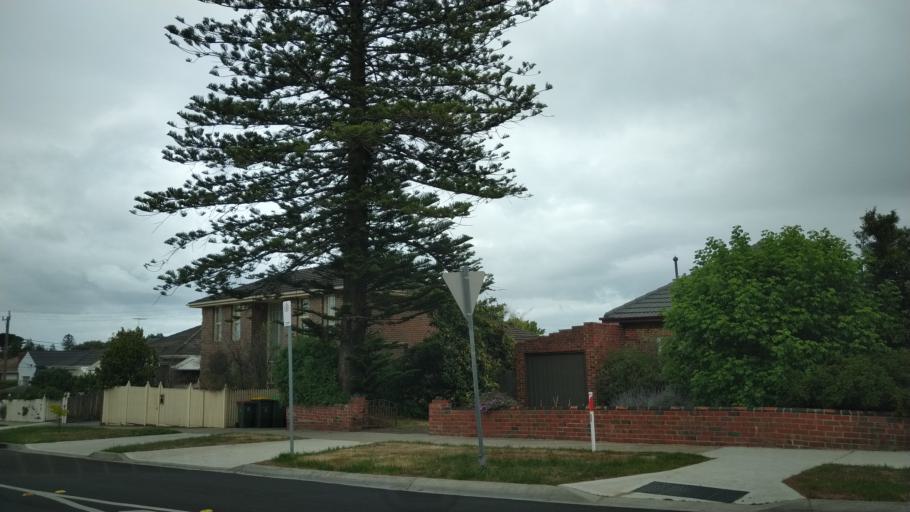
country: AU
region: Victoria
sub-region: Glen Eira
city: Caulfield South
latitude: -37.8955
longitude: 145.0240
